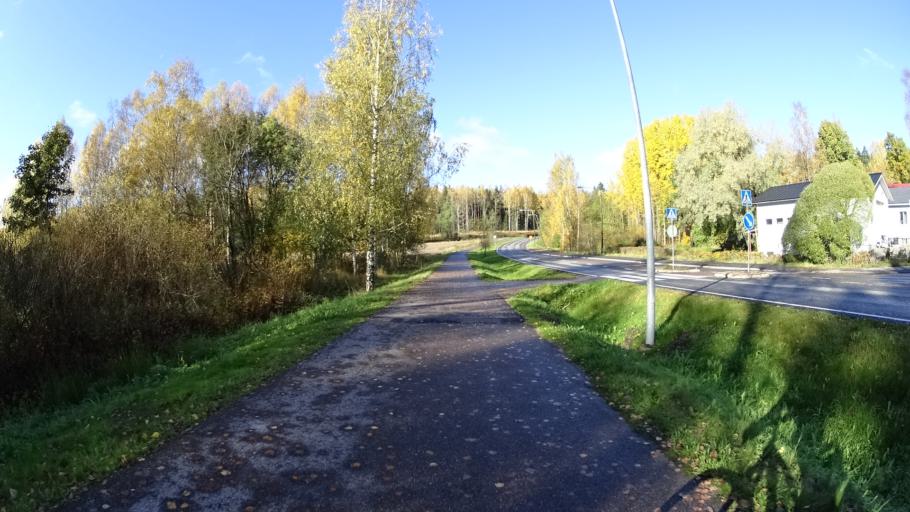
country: FI
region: Uusimaa
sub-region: Helsinki
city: Kilo
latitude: 60.2501
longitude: 24.8022
